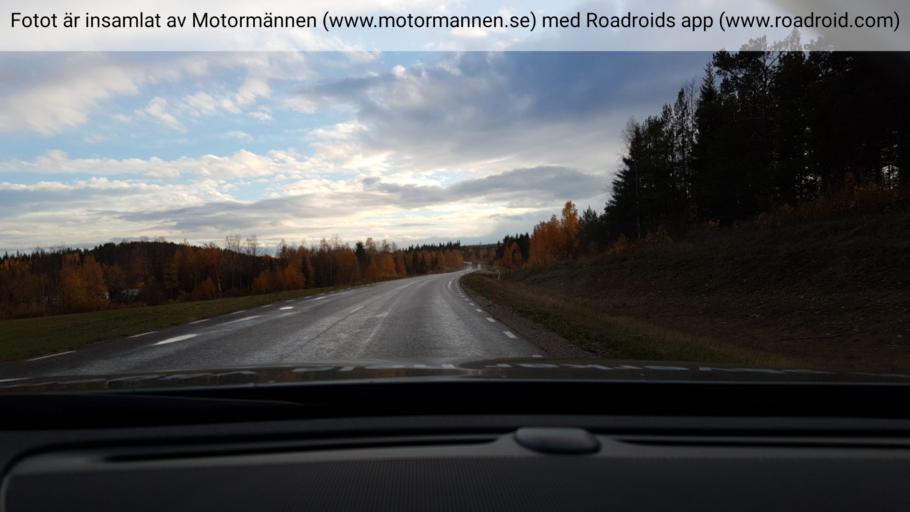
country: SE
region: Norrbotten
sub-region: Overkalix Kommun
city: OEverkalix
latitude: 66.7620
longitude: 22.6830
